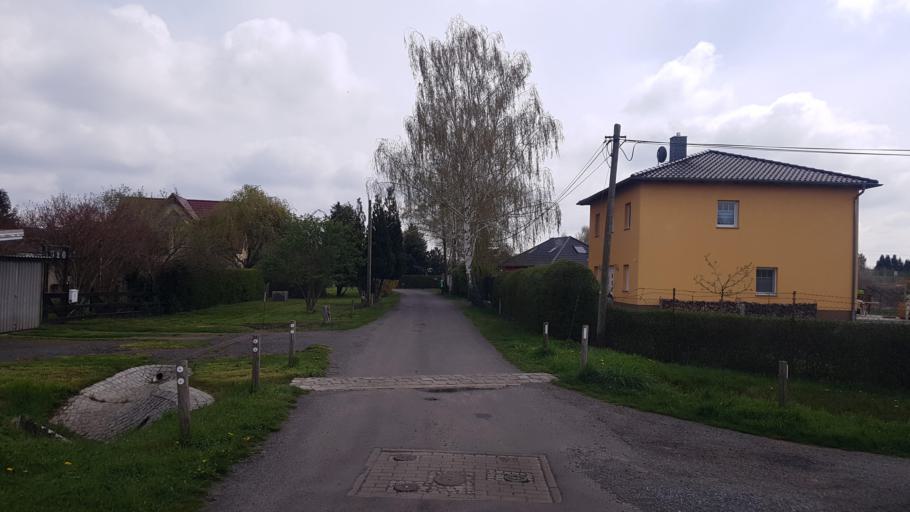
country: DE
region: Brandenburg
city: Luckenwalde
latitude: 52.1013
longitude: 13.1693
